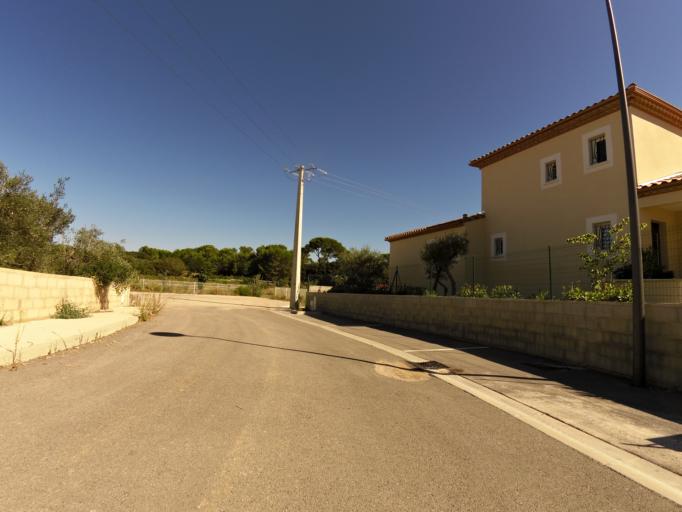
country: FR
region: Languedoc-Roussillon
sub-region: Departement du Gard
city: Aubais
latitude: 43.7565
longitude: 4.1553
